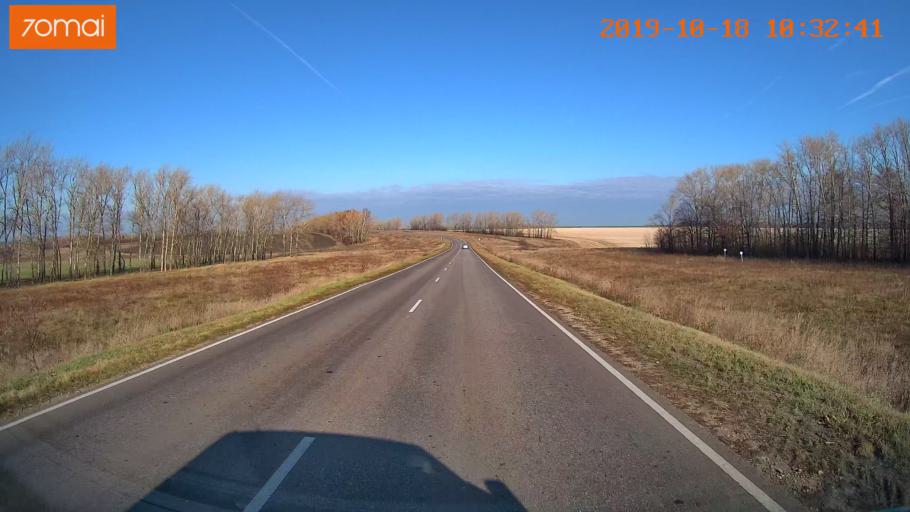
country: RU
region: Tula
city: Kurkino
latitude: 53.4975
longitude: 38.6206
